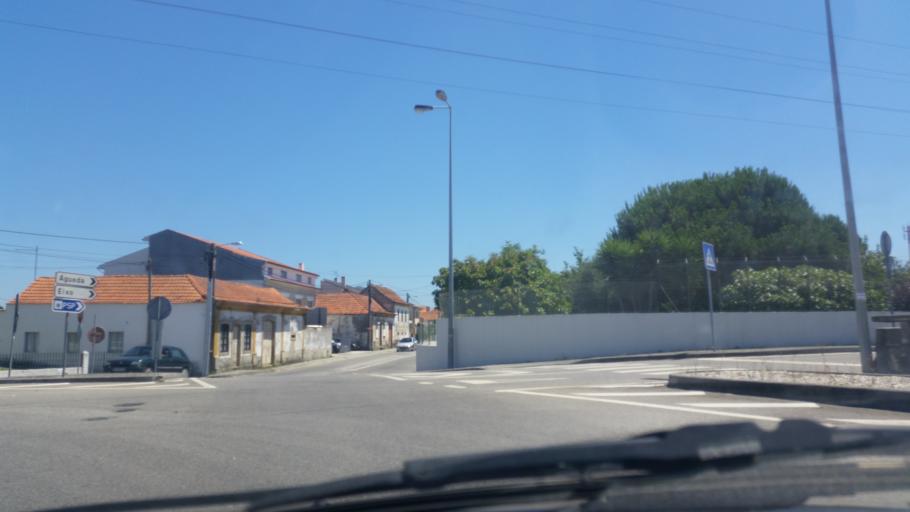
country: PT
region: Aveiro
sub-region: Aveiro
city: Aveiro
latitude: 40.6466
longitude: -8.6262
